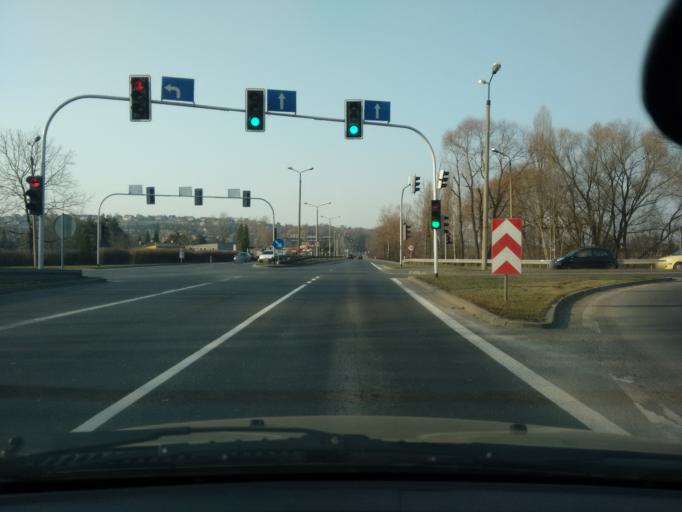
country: PL
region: Silesian Voivodeship
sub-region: Powiat cieszynski
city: Skoczow
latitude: 49.8029
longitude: 18.7908
